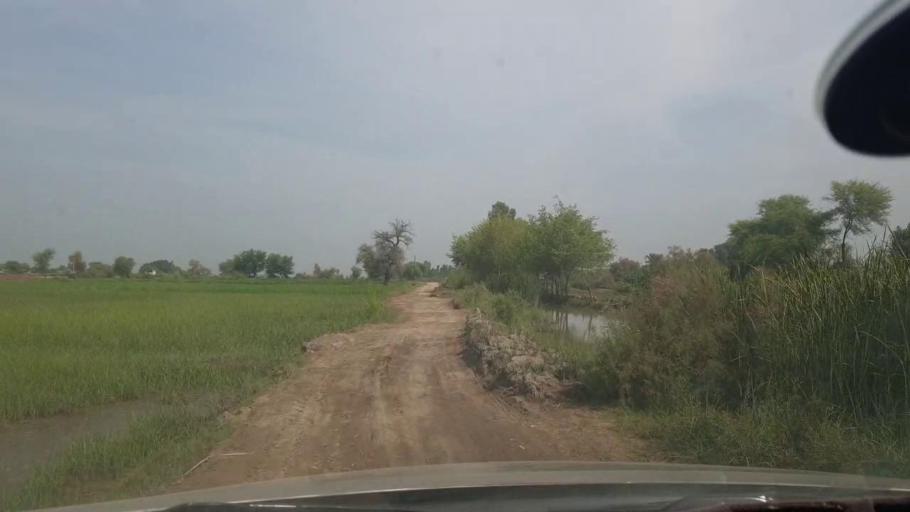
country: PK
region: Sindh
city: Jacobabad
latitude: 28.3138
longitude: 68.4825
